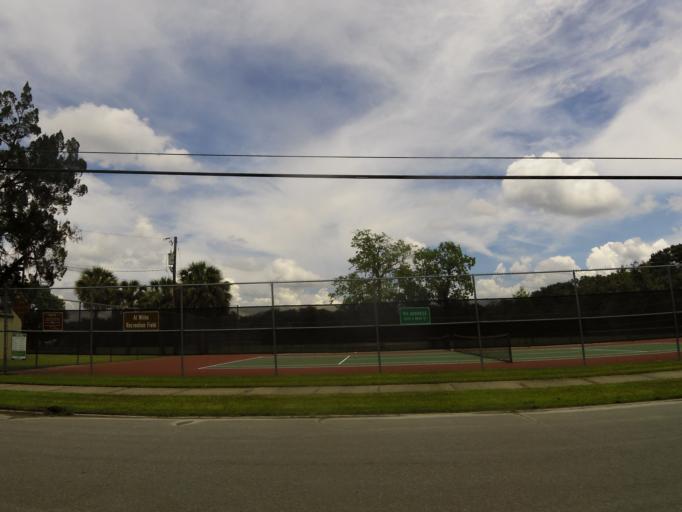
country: US
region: Florida
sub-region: Putnam County
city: East Palatka
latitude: 29.7124
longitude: -81.5080
